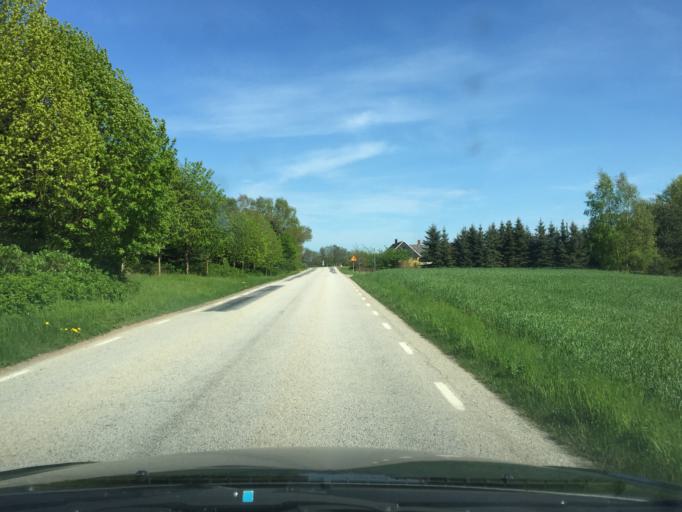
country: SE
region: Skane
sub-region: Sjobo Kommun
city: Blentarp
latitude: 55.5744
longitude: 13.5845
